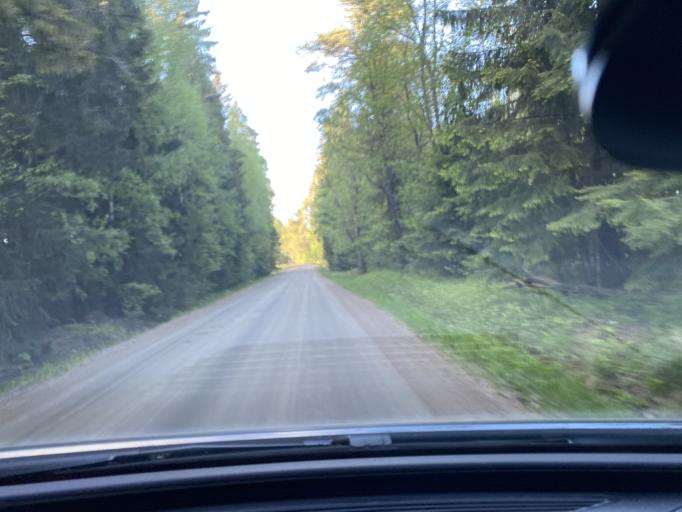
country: FI
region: Satakunta
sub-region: Pori
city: Huittinen
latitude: 61.1373
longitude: 22.8334
